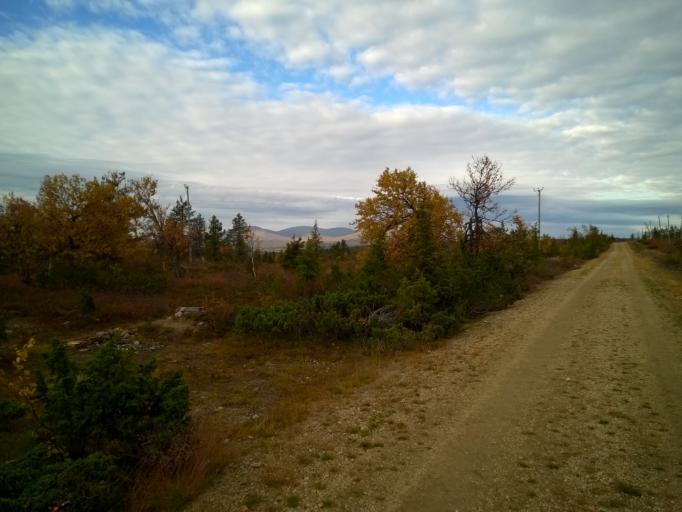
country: FI
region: Lapland
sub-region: Tunturi-Lappi
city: Muonio
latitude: 67.9712
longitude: 24.0969
